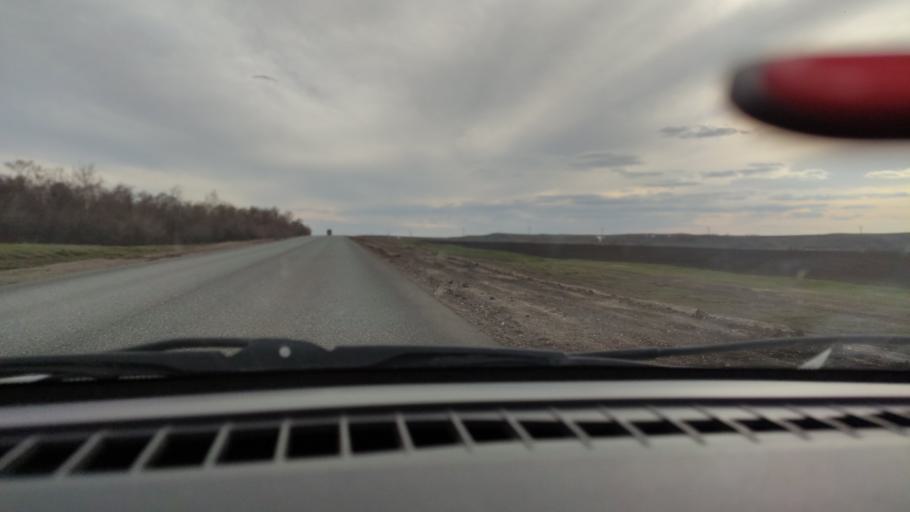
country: RU
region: Bashkortostan
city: Yermolayevo
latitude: 52.4622
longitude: 55.8235
